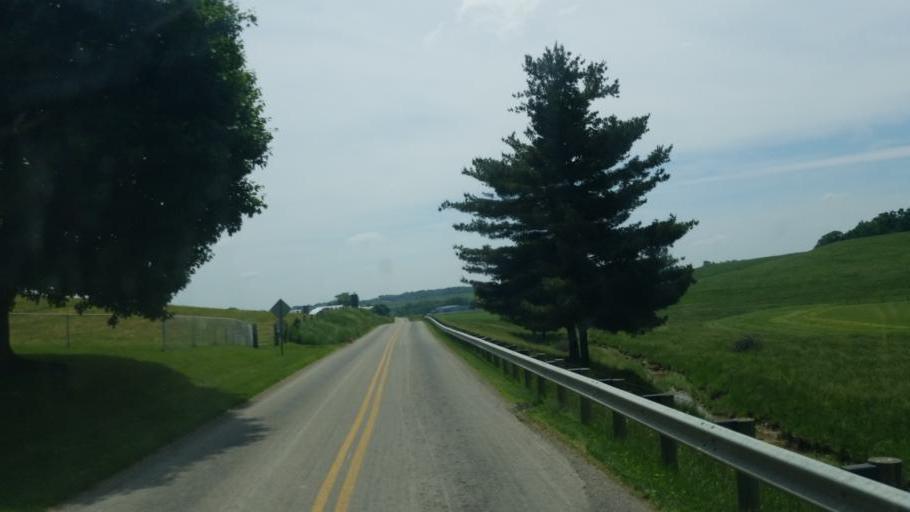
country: US
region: Ohio
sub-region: Tuscarawas County
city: Sugarcreek
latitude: 40.5094
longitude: -81.6851
